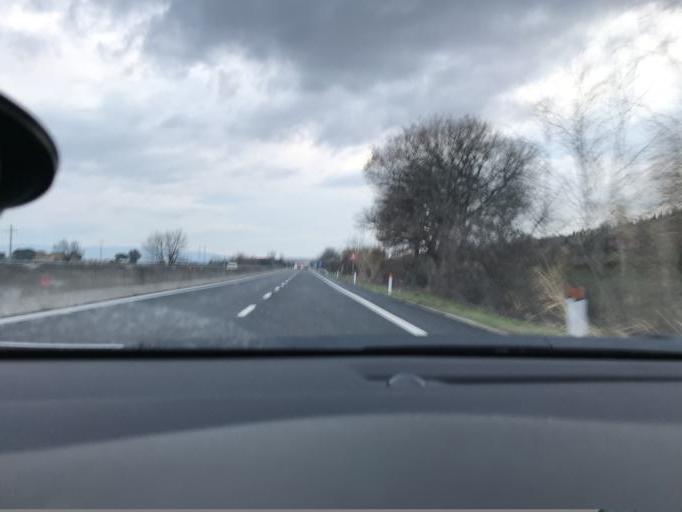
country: IT
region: Umbria
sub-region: Provincia di Perugia
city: Petrignano
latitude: 43.1318
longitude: 12.5224
